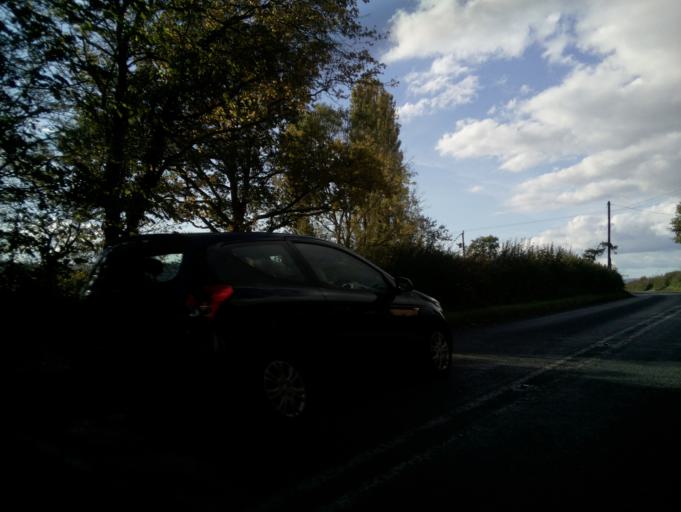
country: GB
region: England
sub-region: Herefordshire
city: Moccas
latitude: 52.1038
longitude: -2.9516
